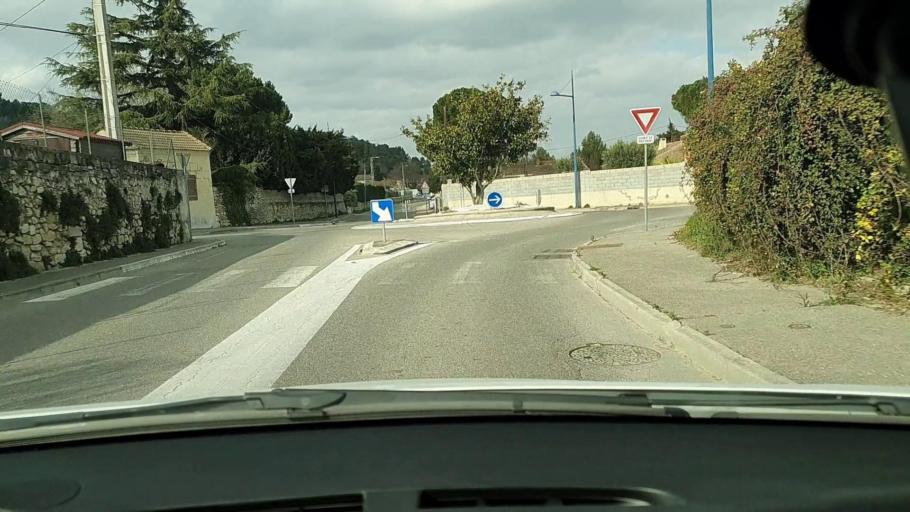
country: FR
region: Languedoc-Roussillon
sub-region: Departement du Gard
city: Beaucaire
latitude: 43.8161
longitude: 4.6303
